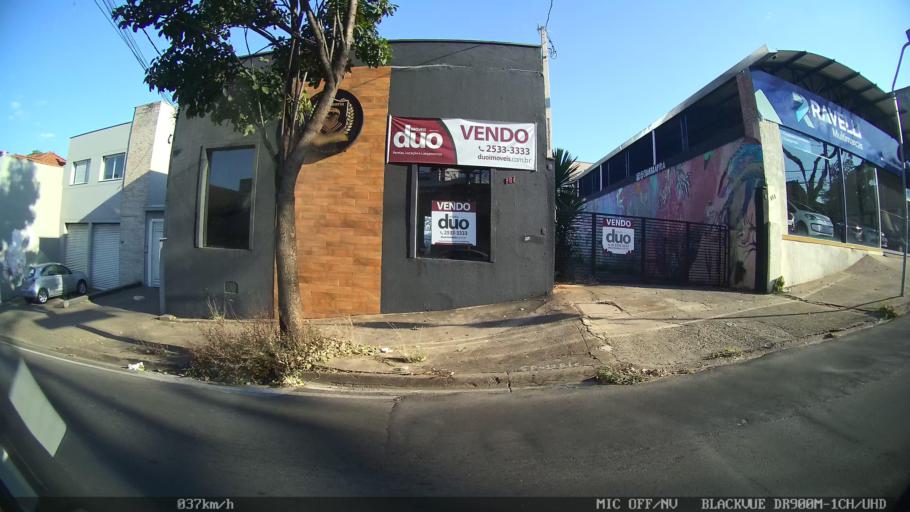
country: BR
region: Sao Paulo
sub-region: Piracicaba
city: Piracicaba
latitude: -22.7135
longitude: -47.6539
